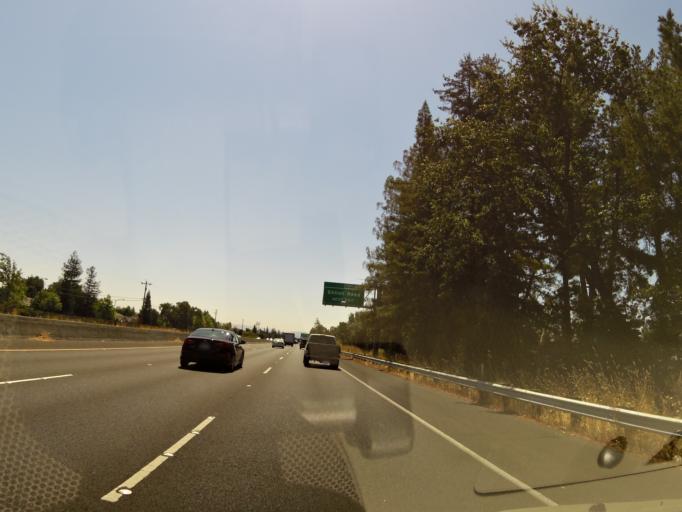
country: US
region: California
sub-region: Sonoma County
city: Windsor
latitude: 38.5325
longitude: -122.7962
